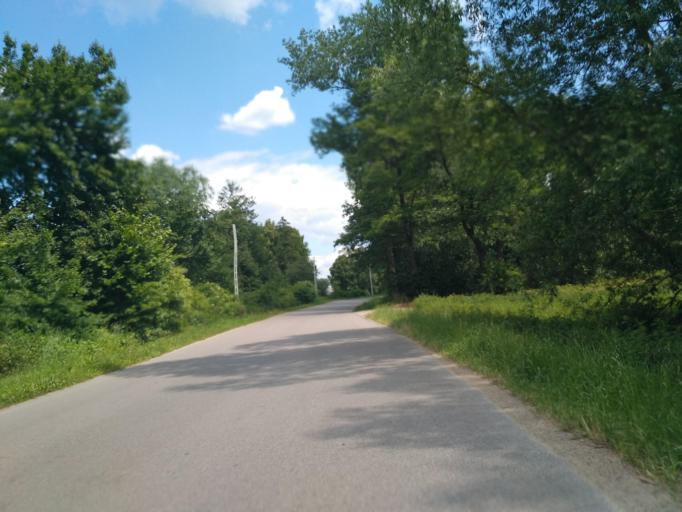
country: PL
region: Subcarpathian Voivodeship
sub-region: Powiat debicki
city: Brzostek
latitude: 49.8616
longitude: 21.4471
